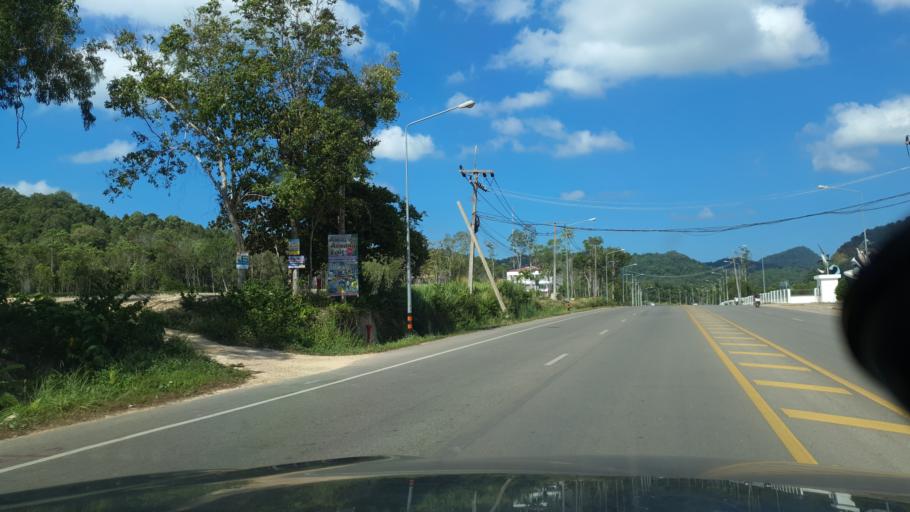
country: TH
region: Phangnga
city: Ban Ao Nang
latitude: 8.0397
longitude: 98.8510
